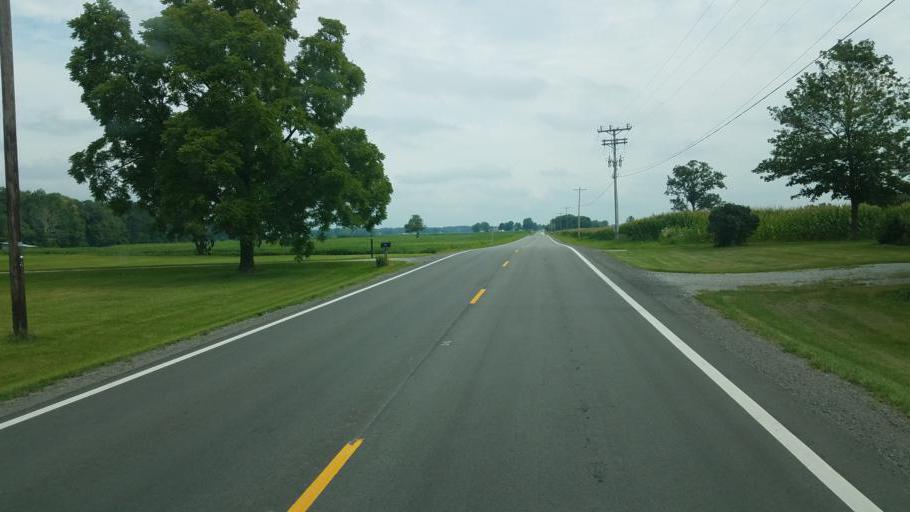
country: US
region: Ohio
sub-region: Marion County
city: Marion
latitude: 40.5278
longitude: -83.0563
